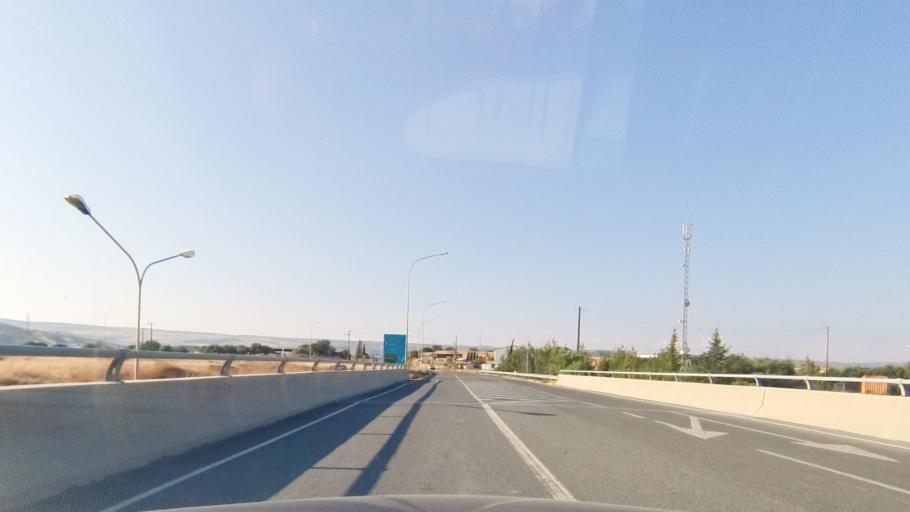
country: CY
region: Limassol
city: Pissouri
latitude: 34.6823
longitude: 32.7604
